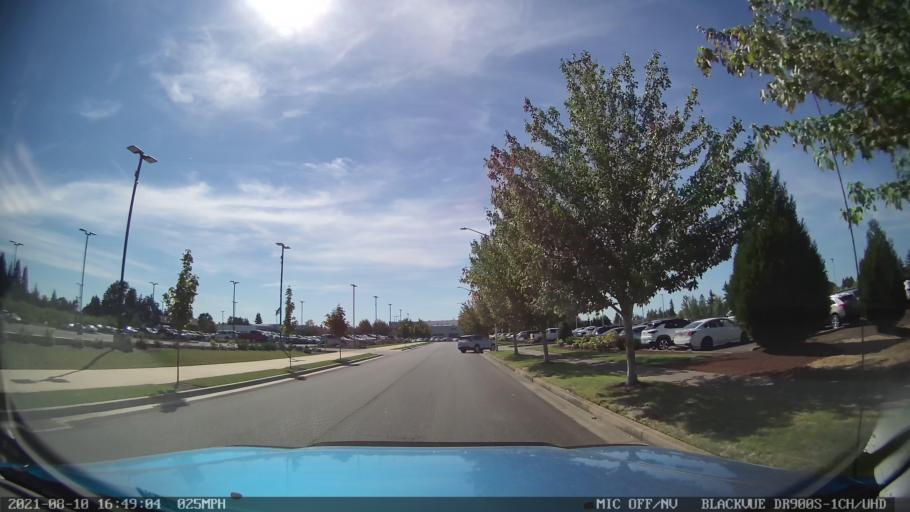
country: US
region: Oregon
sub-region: Marion County
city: Keizer
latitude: 44.9694
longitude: -123.0230
